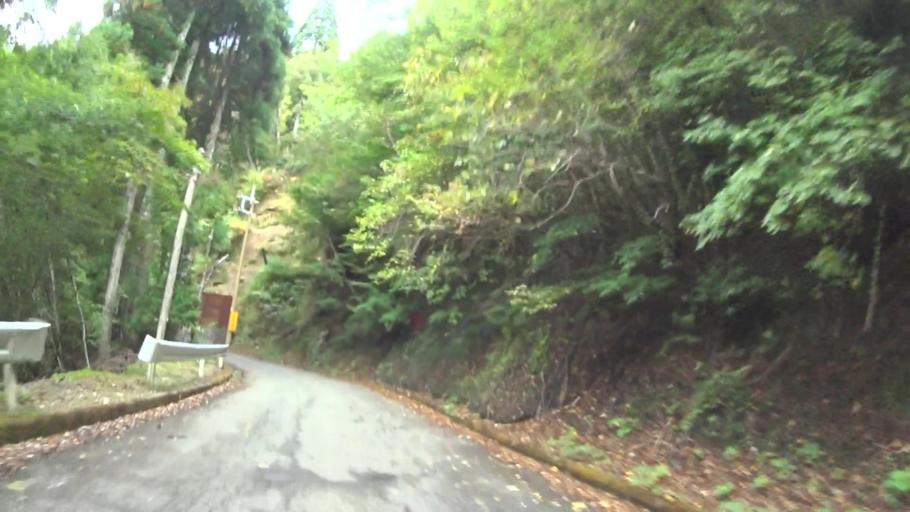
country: JP
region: Shiga Prefecture
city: Kitahama
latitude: 35.2721
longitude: 135.7364
